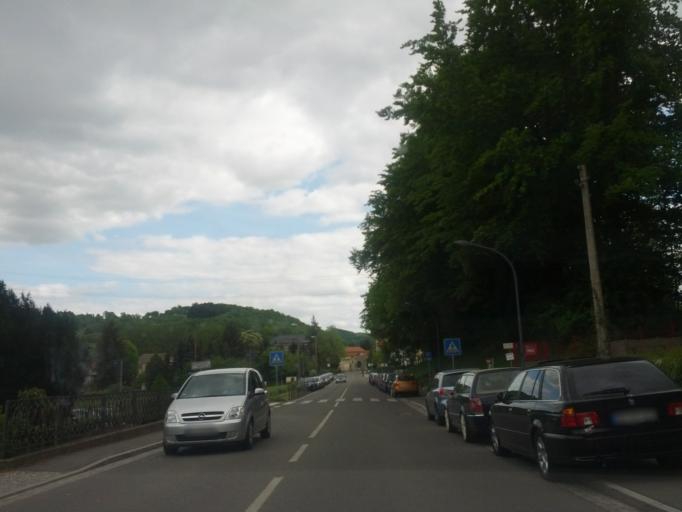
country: DE
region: Saxony
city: Kreischa
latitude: 50.9436
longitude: 13.7633
